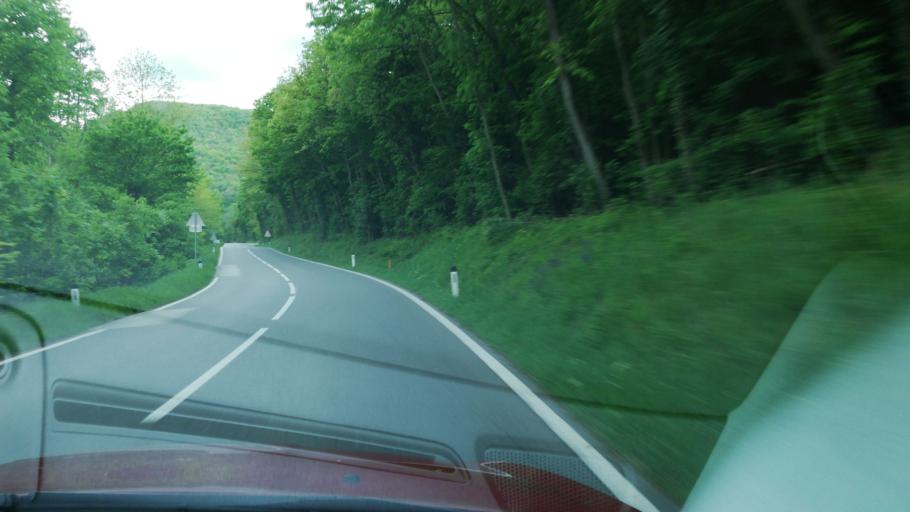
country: AT
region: Lower Austria
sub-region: Politischer Bezirk Modling
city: Gaaden
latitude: 48.0186
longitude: 16.1890
